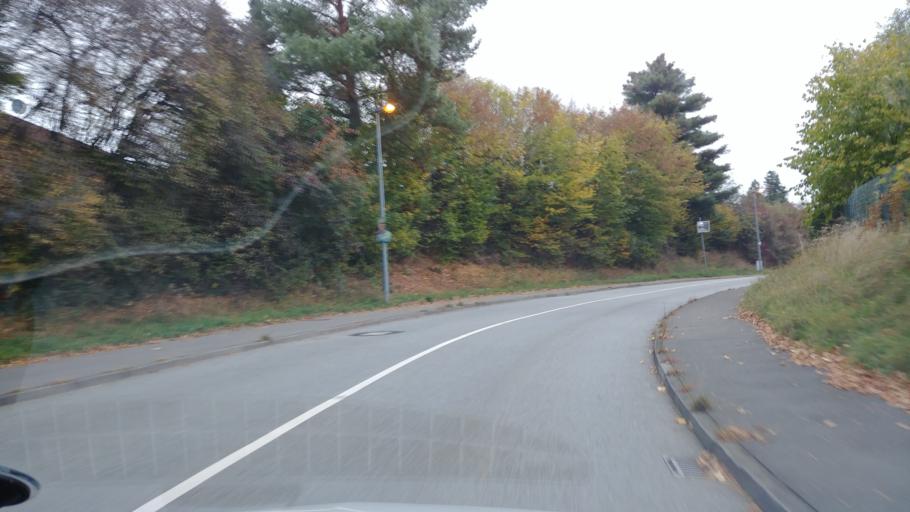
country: DE
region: Hesse
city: Taunusstein
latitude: 50.1480
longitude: 8.1537
